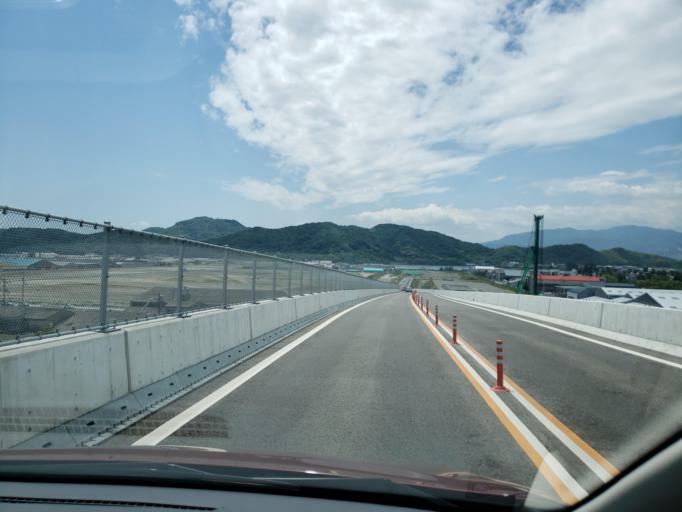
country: JP
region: Tokushima
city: Tokushima-shi
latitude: 34.0481
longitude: 134.5854
